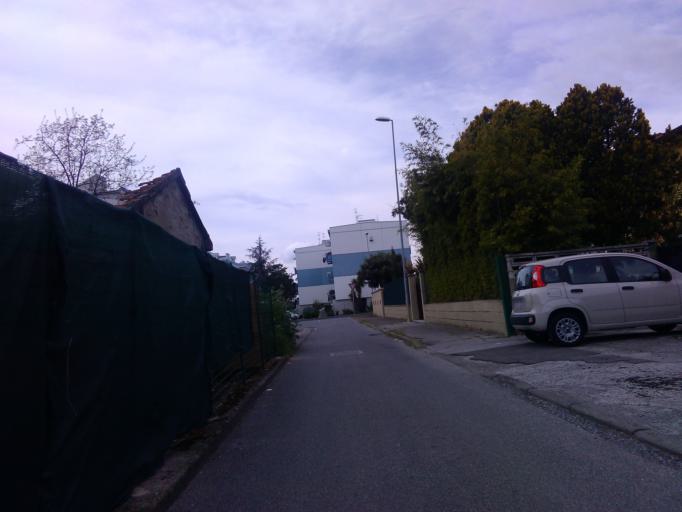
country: IT
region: Tuscany
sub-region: Provincia di Massa-Carrara
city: Carrara
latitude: 44.0542
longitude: 10.0516
